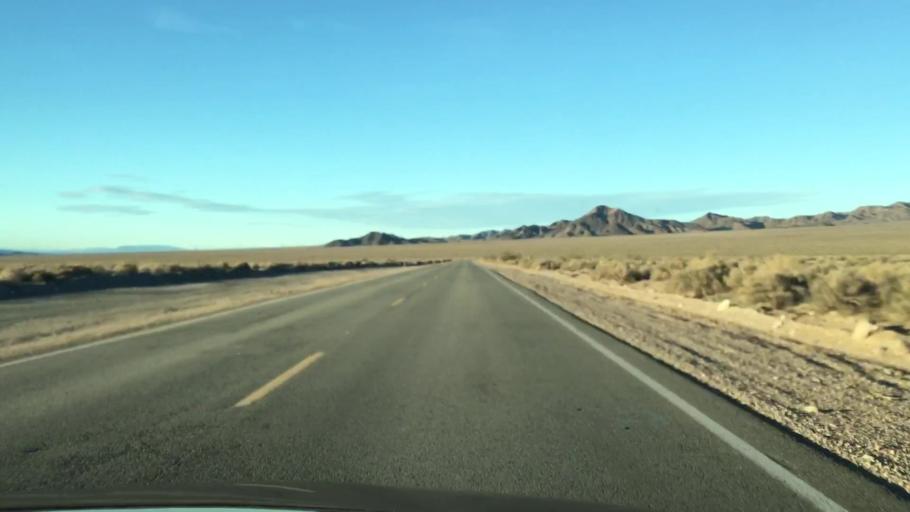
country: US
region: California
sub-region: San Bernardino County
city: Fort Irwin
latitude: 35.3378
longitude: -116.0824
